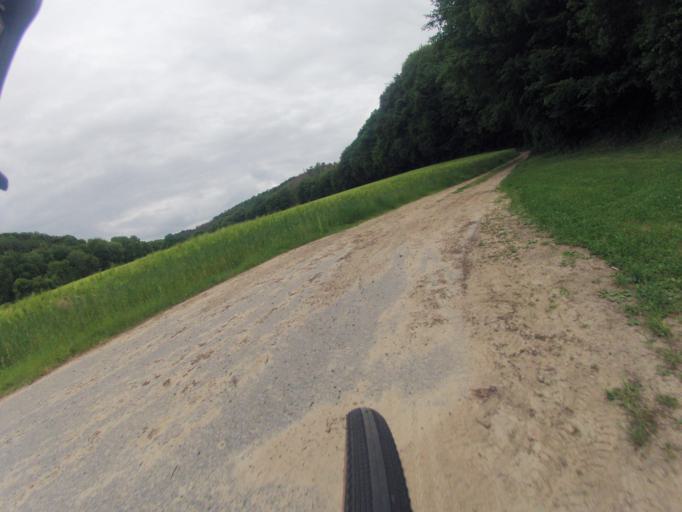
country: DE
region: North Rhine-Westphalia
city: Ibbenburen
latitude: 52.2398
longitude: 7.7394
